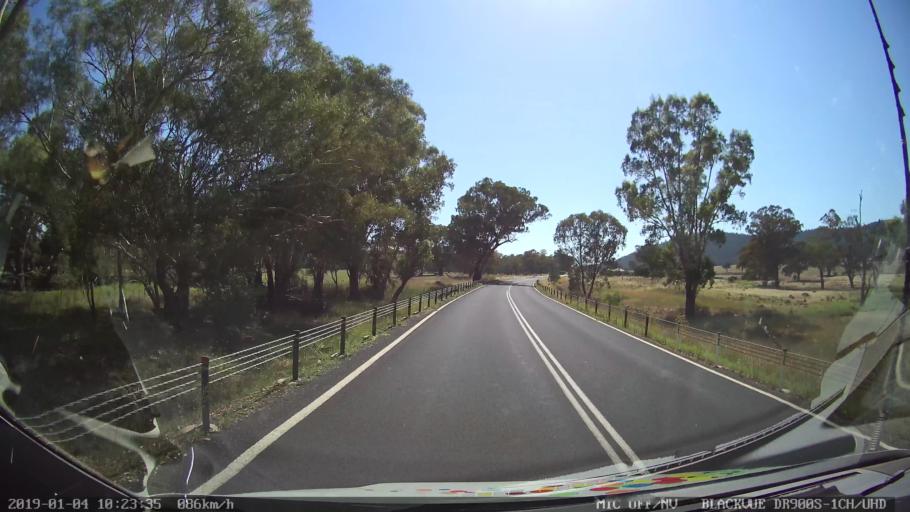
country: AU
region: New South Wales
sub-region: Cabonne
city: Canowindra
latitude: -33.3707
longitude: 148.5414
